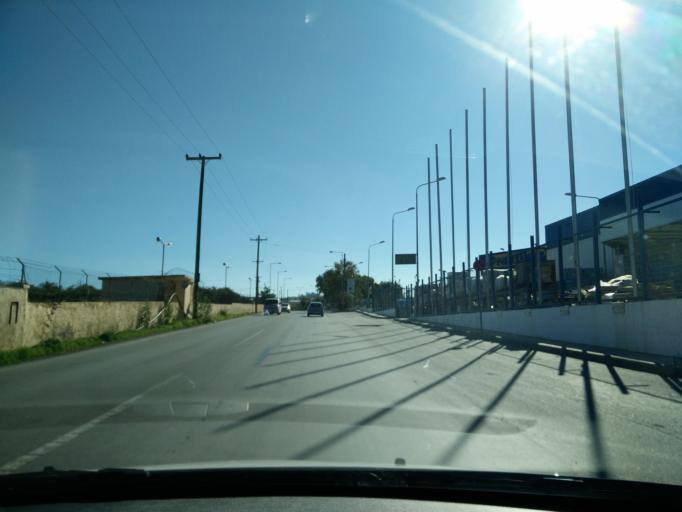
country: GR
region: Crete
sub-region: Nomos Irakleiou
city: Nea Alikarnassos
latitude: 35.3349
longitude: 25.1652
